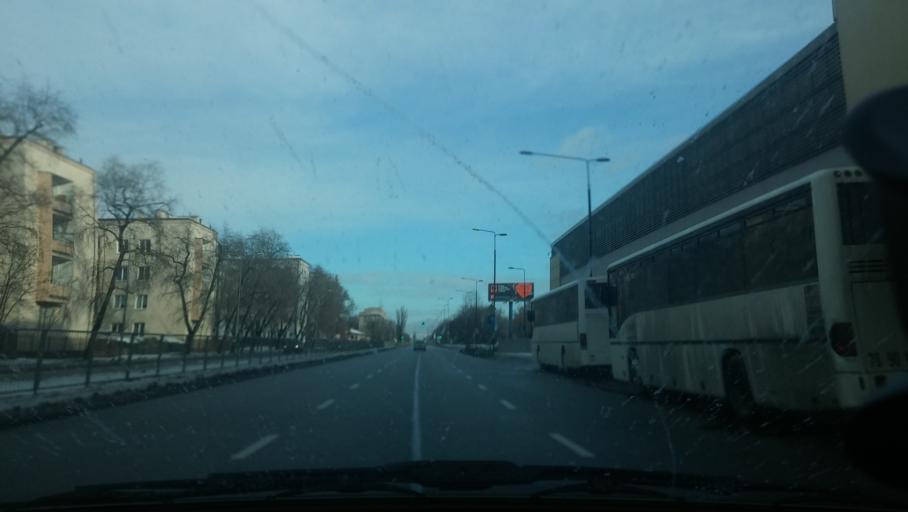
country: PL
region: Masovian Voivodeship
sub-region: Warszawa
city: Praga Polnoc
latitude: 52.2558
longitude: 21.0378
